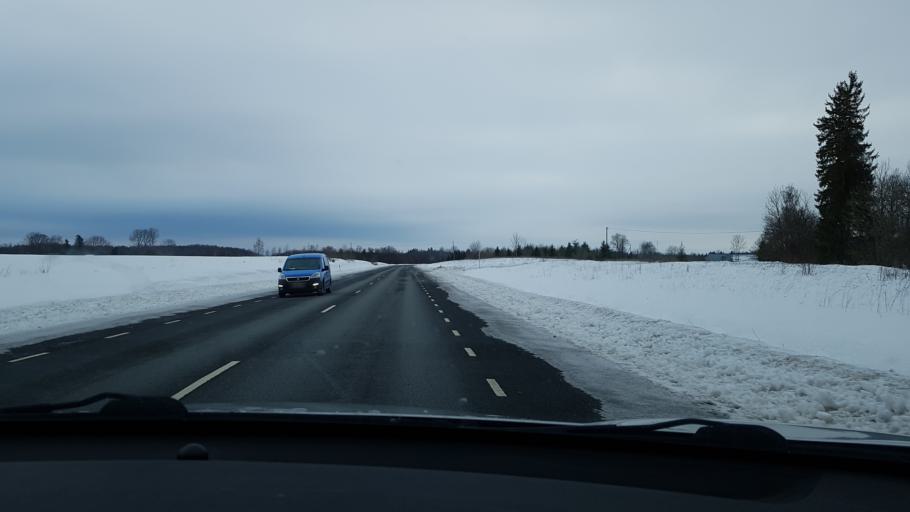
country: EE
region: Jaervamaa
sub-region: Jaerva-Jaani vald
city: Jarva-Jaani
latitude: 58.9002
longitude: 25.8004
